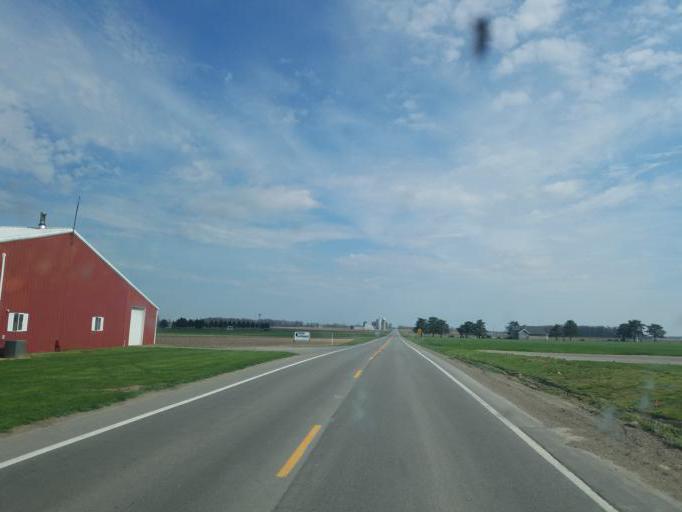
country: US
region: Ohio
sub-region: Crawford County
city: Bucyrus
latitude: 40.7362
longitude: -82.9948
